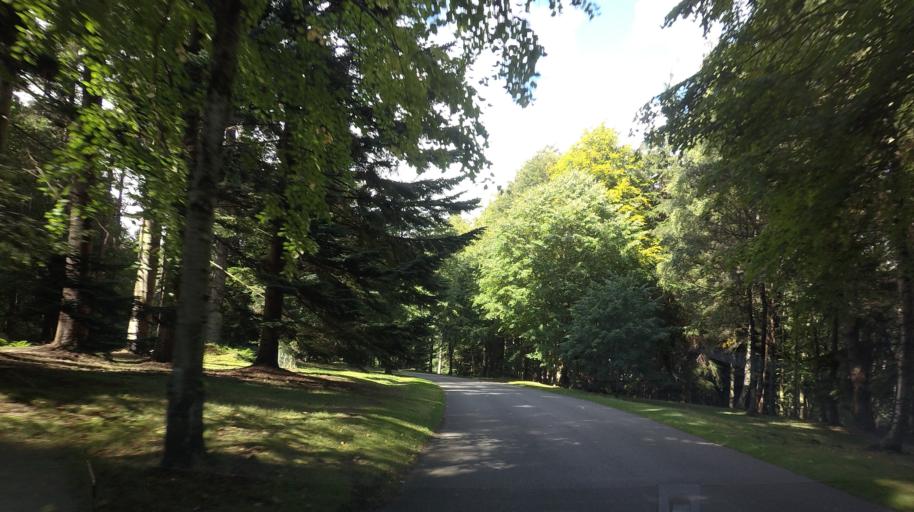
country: GB
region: Scotland
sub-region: Aberdeenshire
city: Banchory
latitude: 57.0590
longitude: -2.4289
